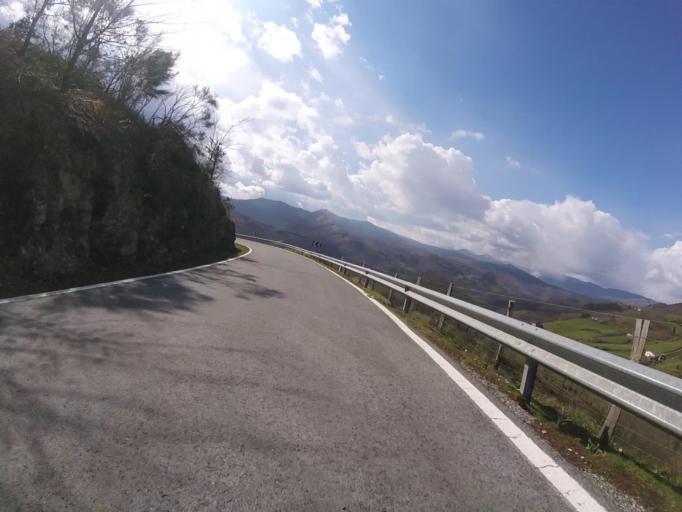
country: ES
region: Navarre
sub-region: Provincia de Navarra
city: Etxalar
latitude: 43.2530
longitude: -1.6162
